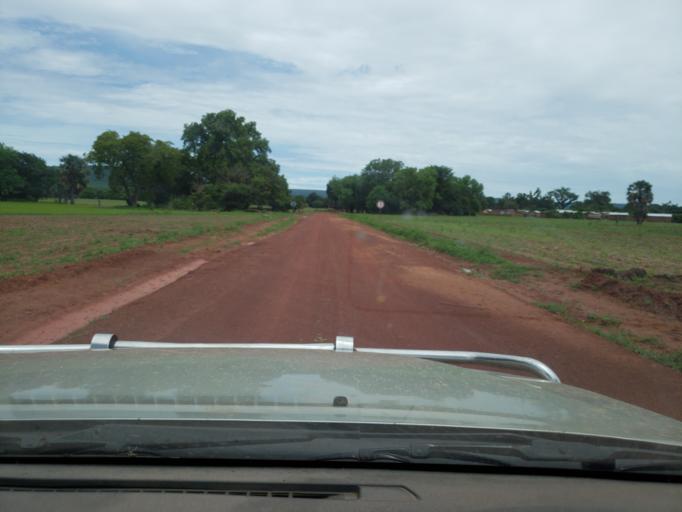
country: ML
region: Sikasso
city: Sikasso
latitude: 11.6735
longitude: -6.3372
